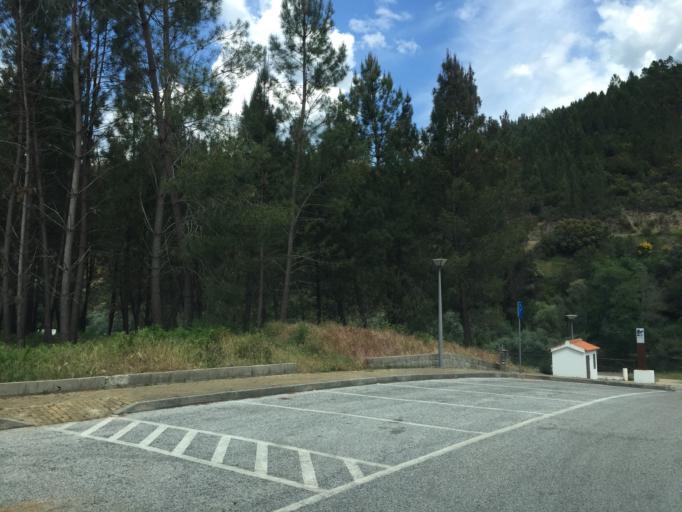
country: PT
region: Coimbra
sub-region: Pampilhosa da Serra
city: Pampilhosa da Serra
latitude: 40.0462
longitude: -7.8021
